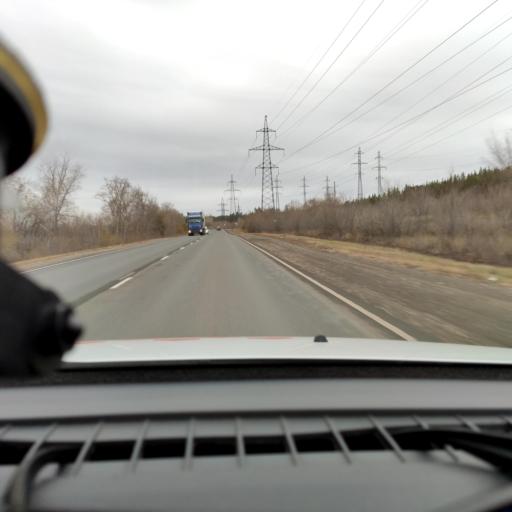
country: RU
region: Samara
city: Samara
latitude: 53.1201
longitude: 50.2159
